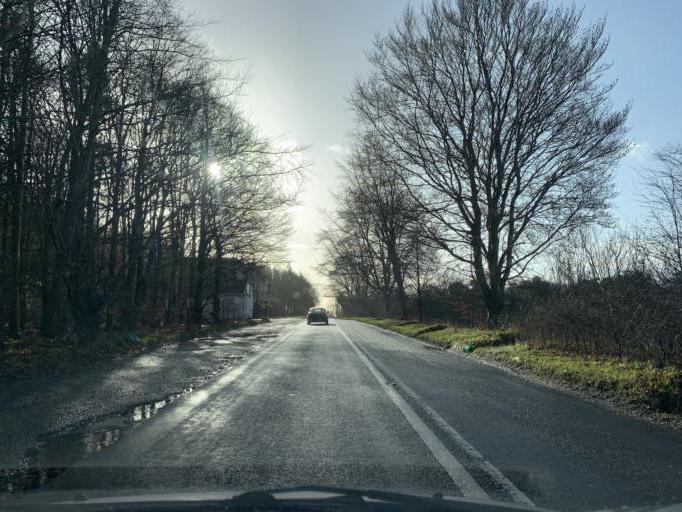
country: GB
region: England
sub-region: Wiltshire
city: Winterbourne Stoke
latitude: 51.1527
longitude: -1.8591
